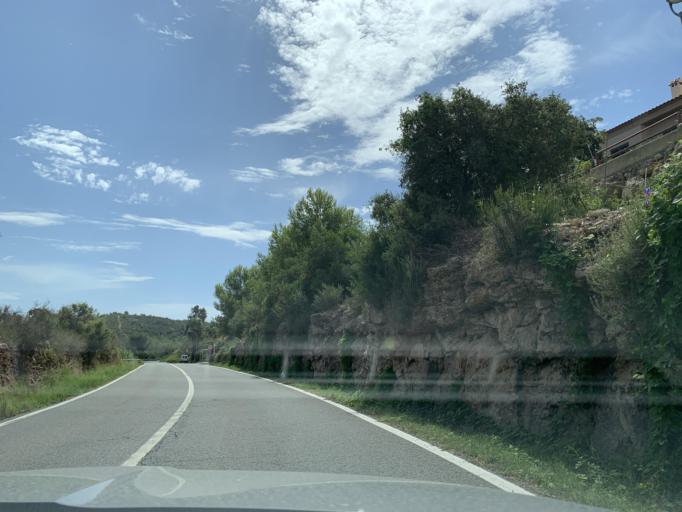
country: ES
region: Catalonia
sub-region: Provincia de Tarragona
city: Altafulla
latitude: 41.1581
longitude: 1.3631
